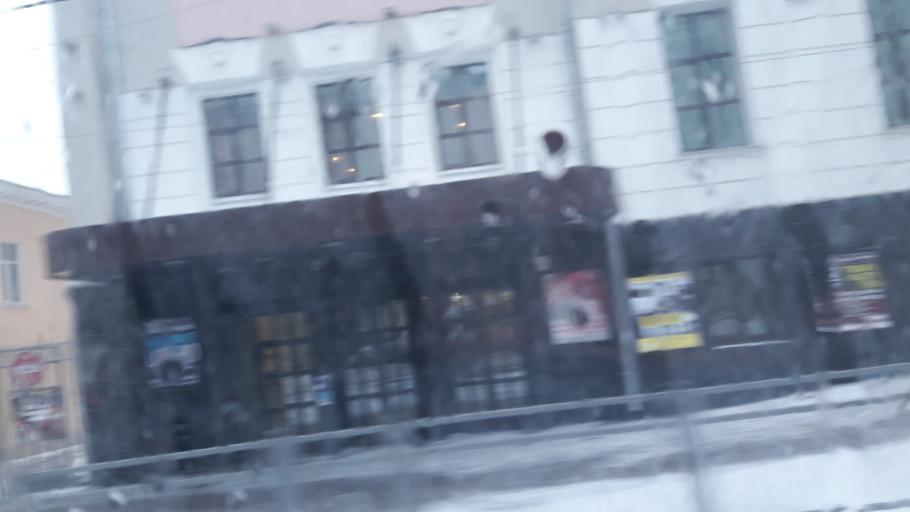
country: RU
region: Tula
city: Tula
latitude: 54.1858
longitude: 37.6097
